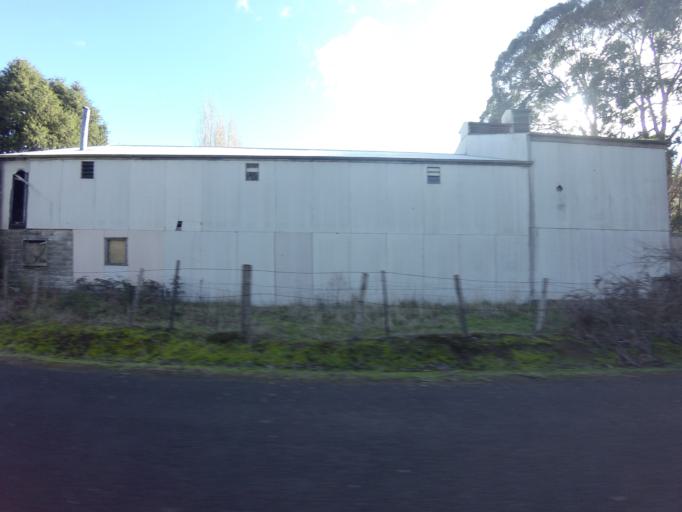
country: AU
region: Tasmania
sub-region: Glenorchy
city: Granton
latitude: -42.8043
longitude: 147.1545
